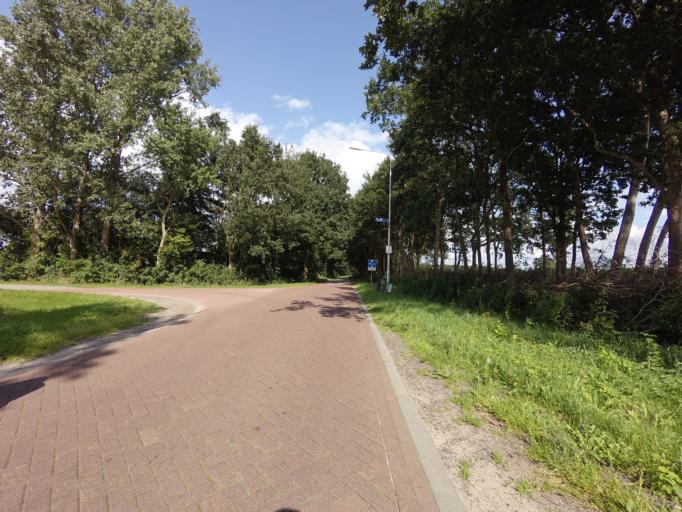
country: NL
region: Friesland
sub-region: Gemeente Heerenveen
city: Jubbega
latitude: 52.9903
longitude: 6.2270
